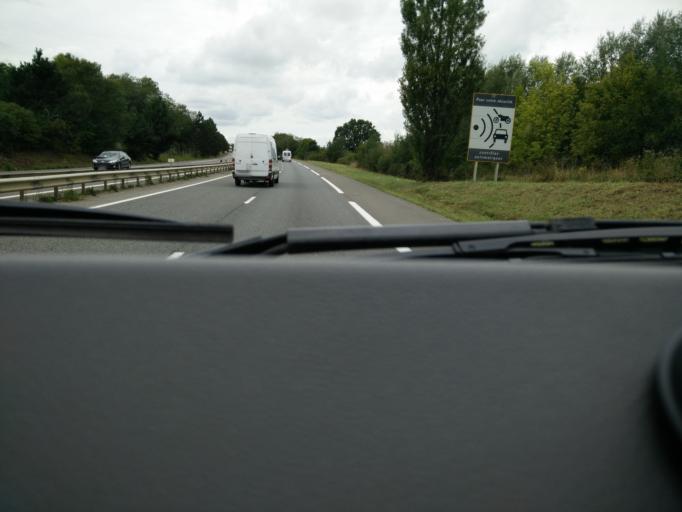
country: FR
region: Champagne-Ardenne
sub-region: Departement des Ardennes
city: Sedan
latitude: 49.6905
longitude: 4.9243
